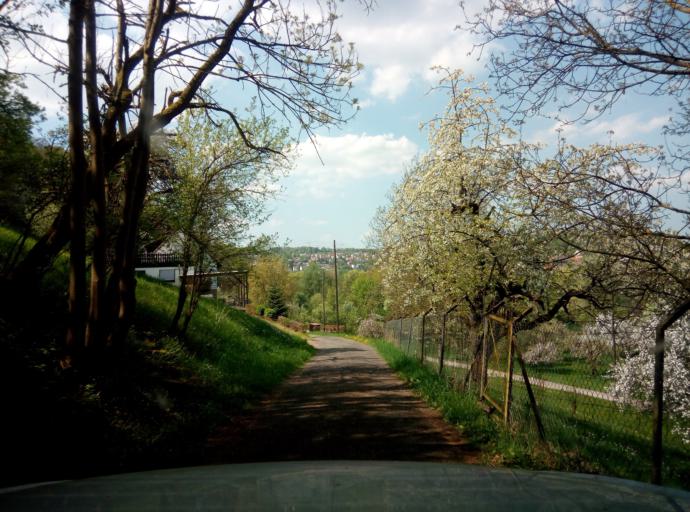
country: DE
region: Baden-Wuerttemberg
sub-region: Tuebingen Region
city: Tuebingen
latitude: 48.5252
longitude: 9.0781
